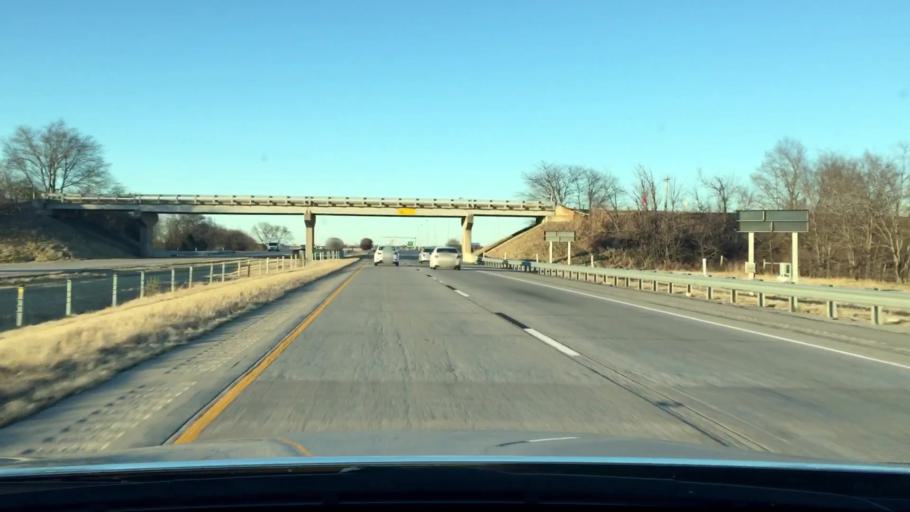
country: US
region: Oklahoma
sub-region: Love County
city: Marietta
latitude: 33.8963
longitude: -97.1344
